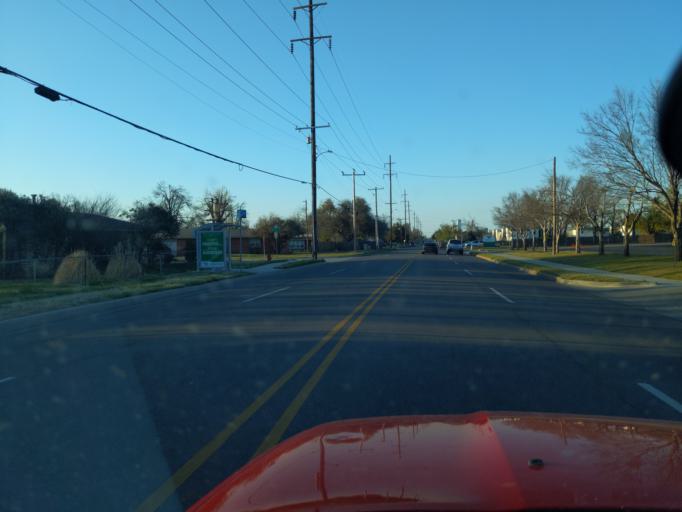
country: US
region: Oklahoma
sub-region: Oklahoma County
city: Oklahoma City
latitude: 35.4072
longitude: -97.5213
